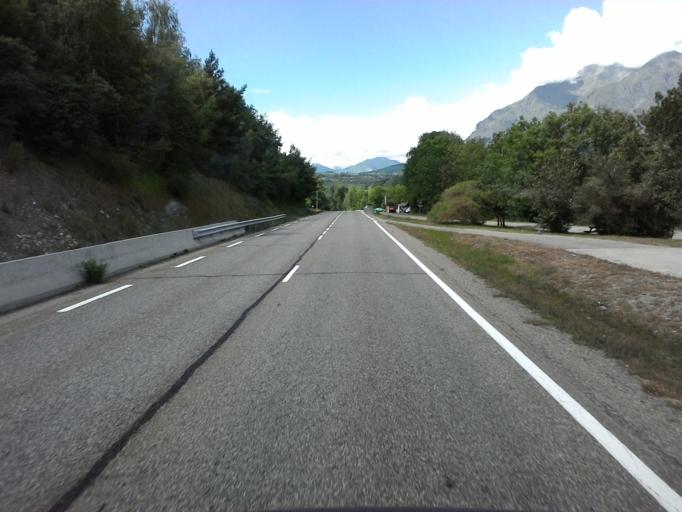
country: FR
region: Provence-Alpes-Cote d'Azur
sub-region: Departement des Hautes-Alpes
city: Saint-Bonnet-en-Champsaur
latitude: 44.6896
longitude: 6.0636
